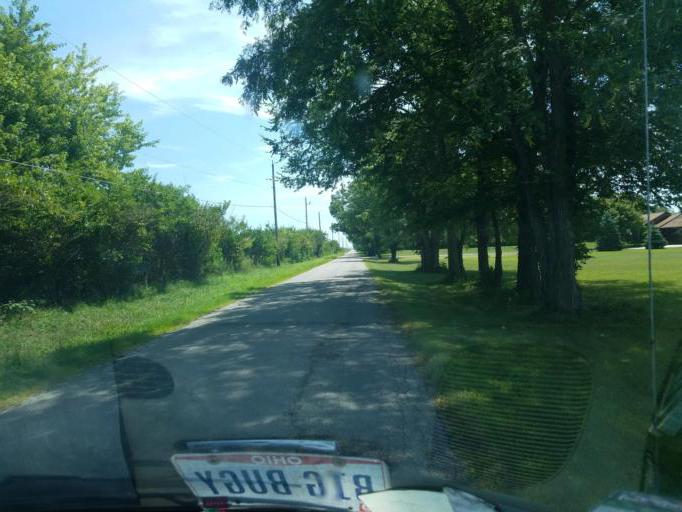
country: US
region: Ohio
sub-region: Franklin County
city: Lake Darby
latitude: 39.8745
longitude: -83.2081
